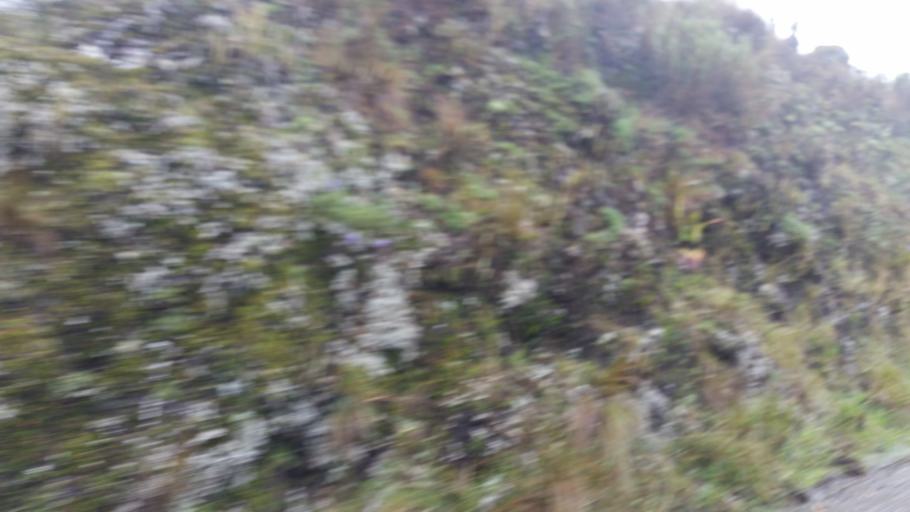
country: CO
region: Cundinamarca
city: La Calera
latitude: 4.6899
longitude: -73.8010
